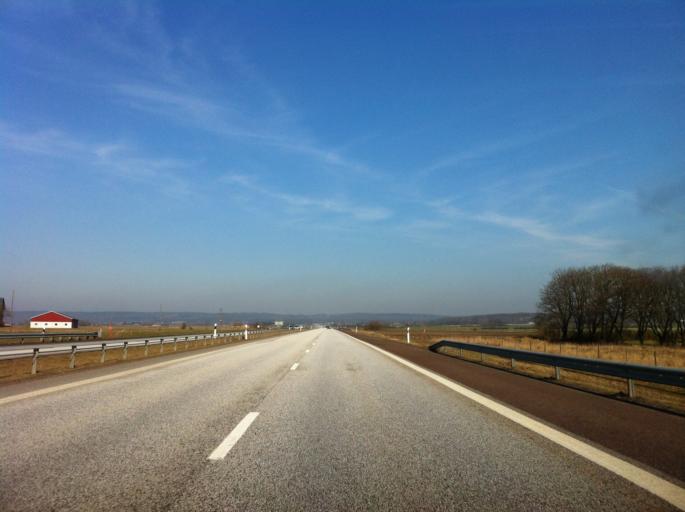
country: SE
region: Skane
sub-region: Angelholms Kommun
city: AEngelholm
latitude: 56.2810
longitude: 12.8982
